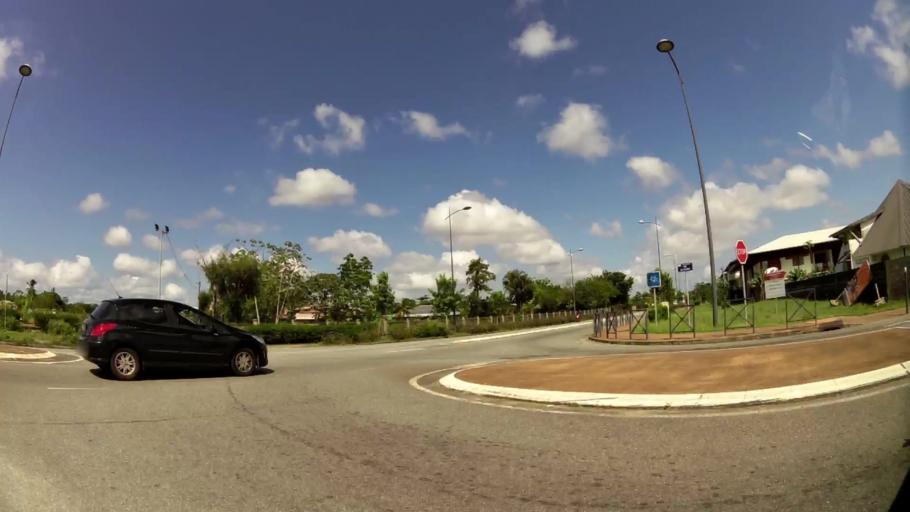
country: GF
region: Guyane
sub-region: Guyane
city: Cayenne
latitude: 4.9185
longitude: -52.3154
